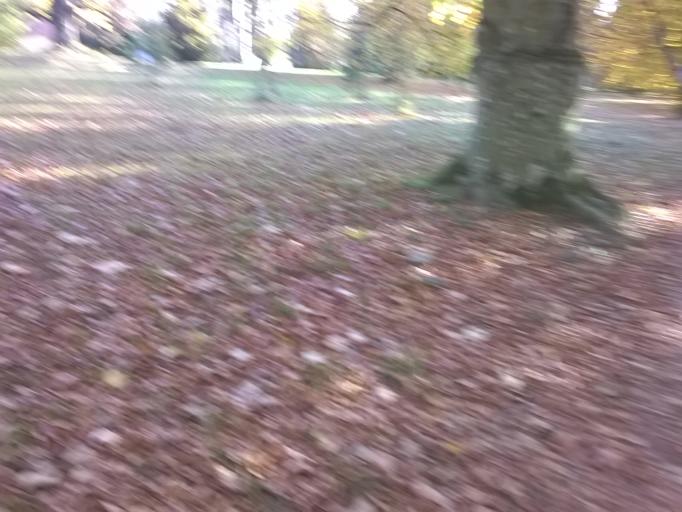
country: SK
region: Nitriansky
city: Zlate Moravce
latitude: 48.4237
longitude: 18.4131
